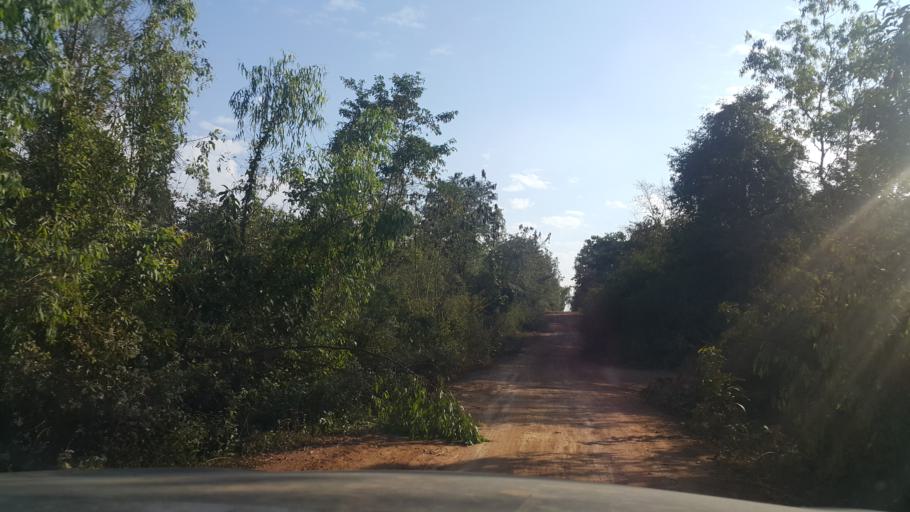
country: TH
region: Lampang
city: Hang Chat
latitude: 18.2816
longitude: 99.3573
